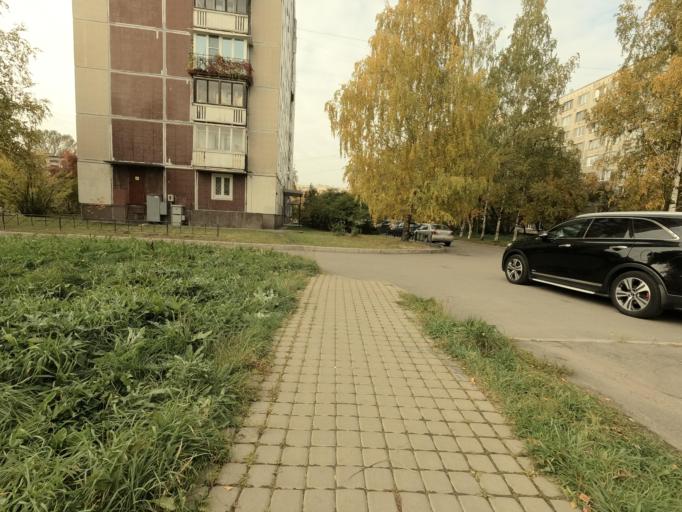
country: RU
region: St.-Petersburg
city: Kupchino
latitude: 59.8536
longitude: 30.3718
